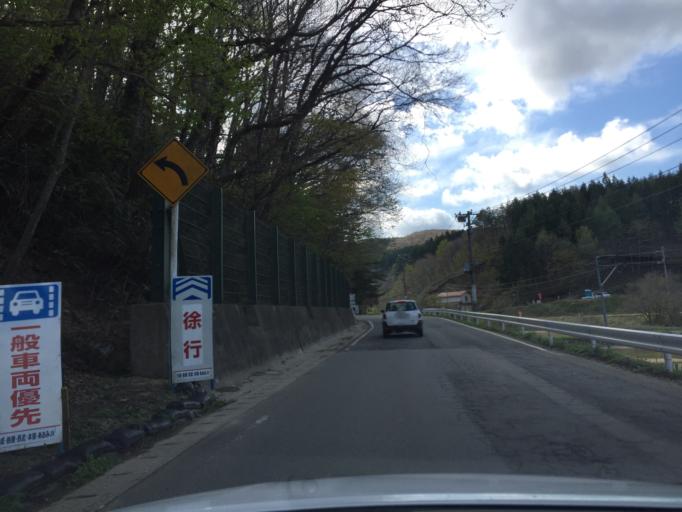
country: JP
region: Fukushima
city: Funehikimachi-funehiki
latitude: 37.5869
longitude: 140.6915
